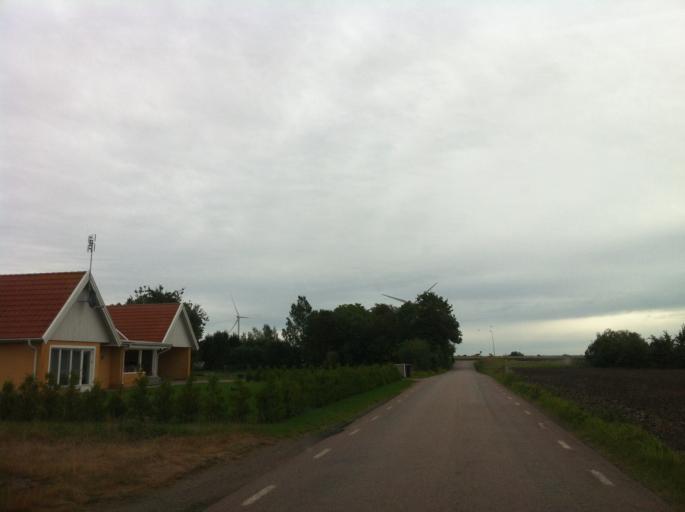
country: SE
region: Skane
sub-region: Svalovs Kommun
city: Teckomatorp
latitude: 55.9008
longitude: 13.0169
